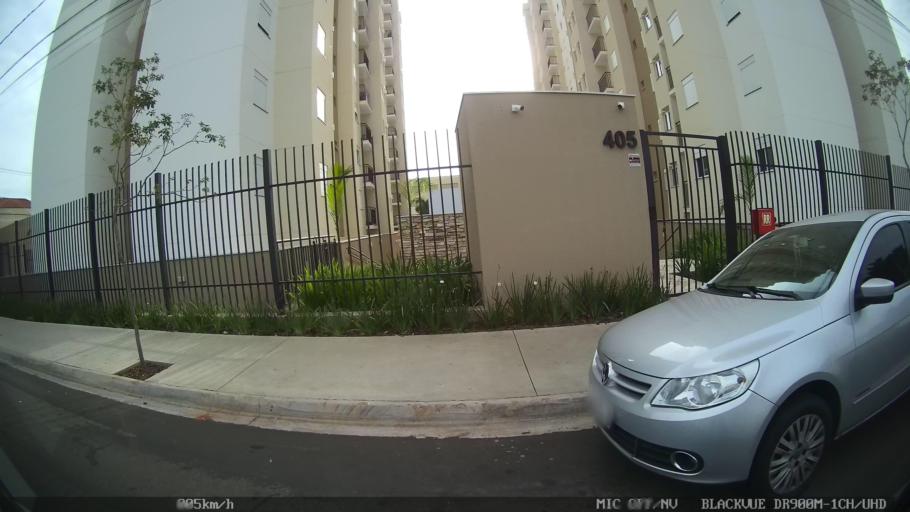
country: BR
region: Sao Paulo
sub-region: Piracicaba
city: Piracicaba
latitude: -22.7353
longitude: -47.6271
